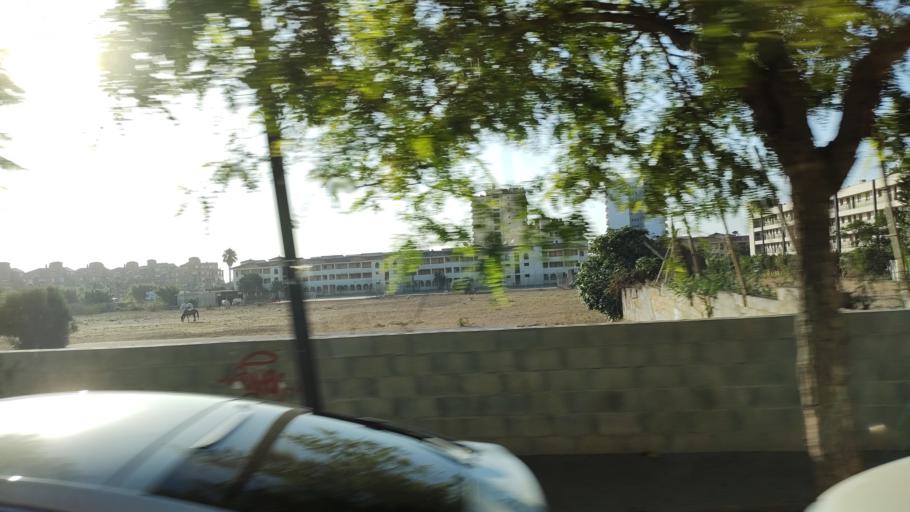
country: ES
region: Andalusia
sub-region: Provincia de Malaga
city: Torremolinos
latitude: 36.6390
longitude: -4.4885
